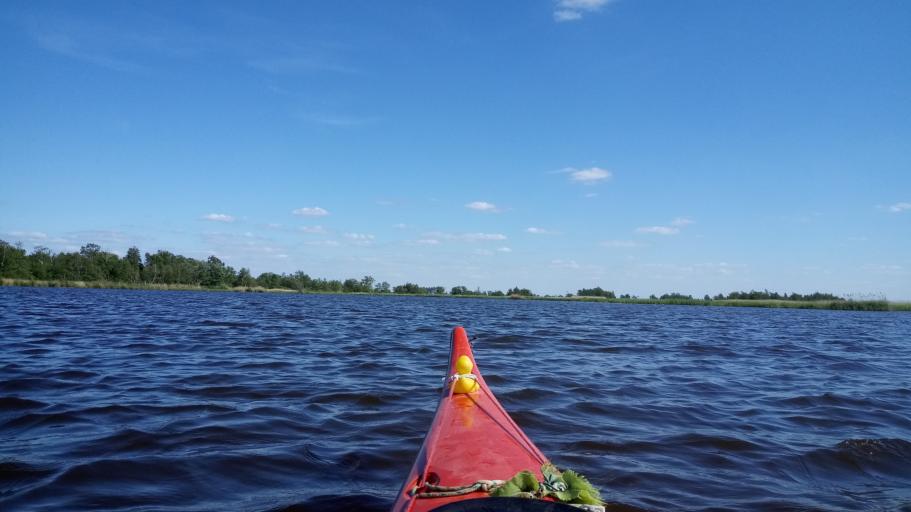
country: NL
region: South Holland
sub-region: Gemeente Nieuwkoop
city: Nieuwkoop
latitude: 52.1548
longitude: 4.8173
